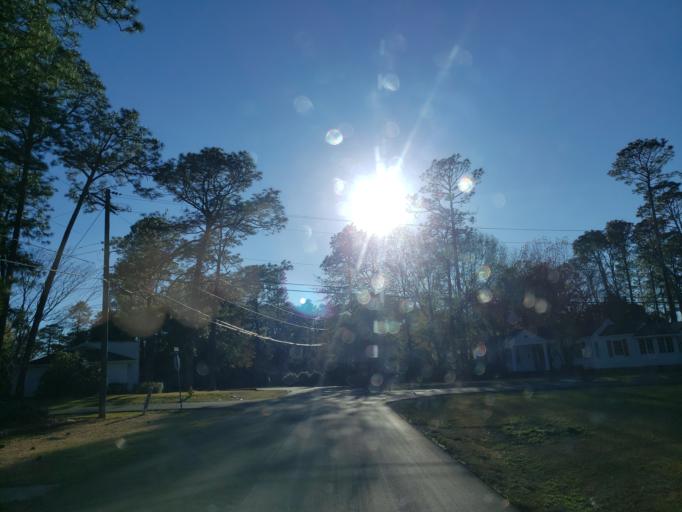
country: US
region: Mississippi
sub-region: Forrest County
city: Hattiesburg
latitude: 31.3151
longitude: -89.3210
